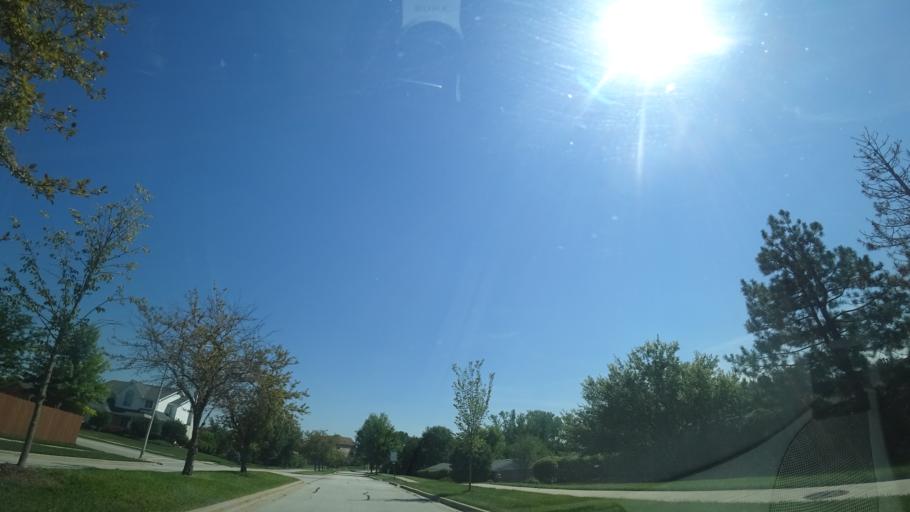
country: US
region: Illinois
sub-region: Will County
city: Mokena
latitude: 41.5629
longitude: -87.8970
